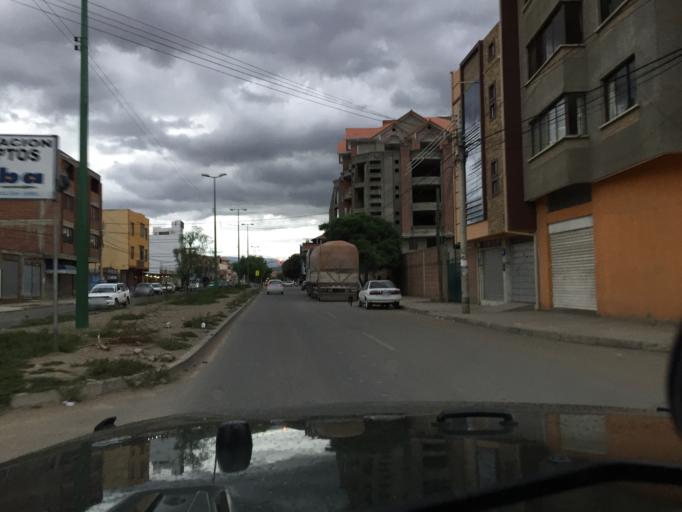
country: BO
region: Cochabamba
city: Cochabamba
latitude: -17.3972
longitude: -66.1992
